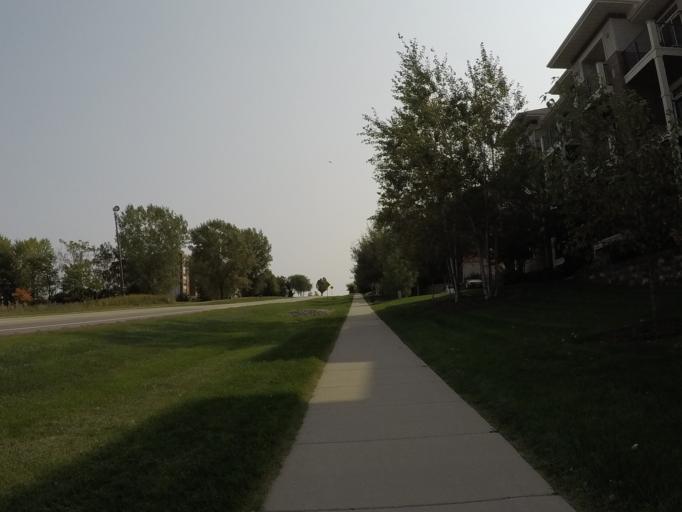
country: US
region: Wisconsin
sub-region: Dane County
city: Verona
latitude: 43.0311
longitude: -89.5490
